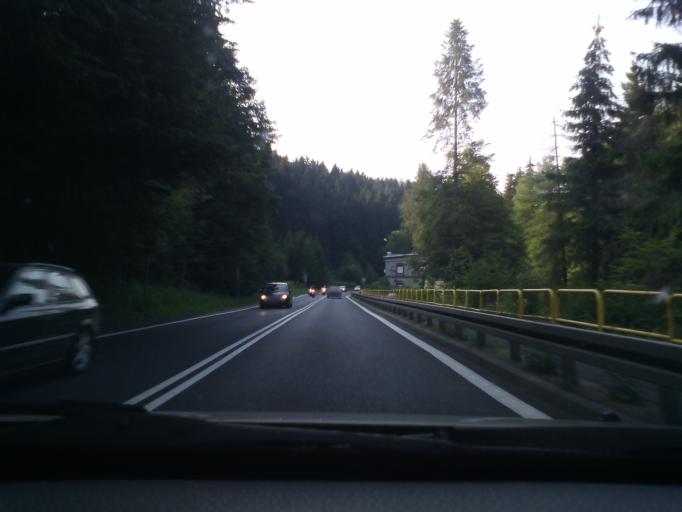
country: PL
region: Lower Silesian Voivodeship
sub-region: Powiat jeleniogorski
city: Piechowice
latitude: 50.8379
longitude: 15.5684
